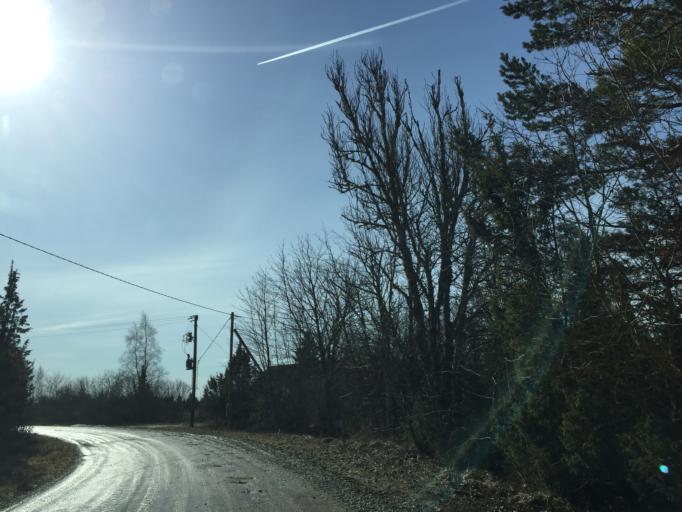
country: EE
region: Laeaene
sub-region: Haapsalu linn
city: Haapsalu
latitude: 58.6826
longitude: 23.5287
